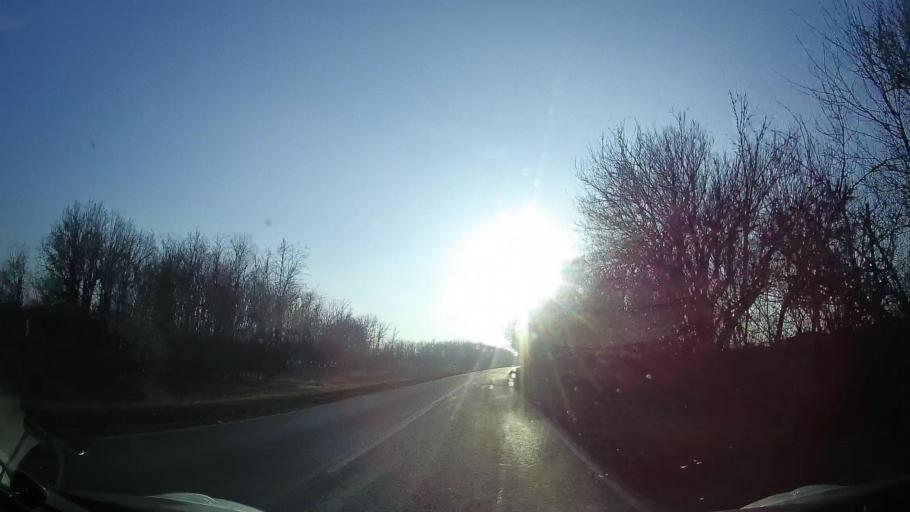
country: RU
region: Rostov
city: Ol'ginskaya
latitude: 47.1638
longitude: 39.9357
